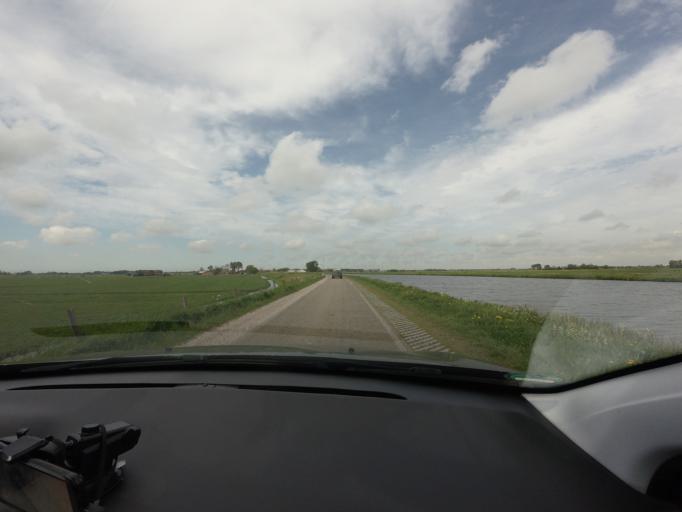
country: NL
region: North Holland
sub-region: Gemeente Zaanstad
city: Zaanstad
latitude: 52.5409
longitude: 4.8290
